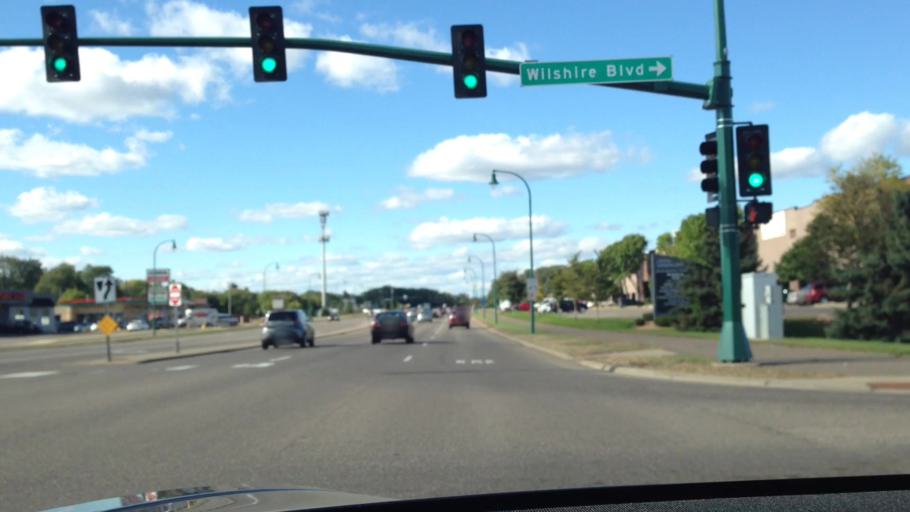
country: US
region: Minnesota
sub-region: Hennepin County
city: Crystal
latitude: 45.0513
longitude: -93.3548
